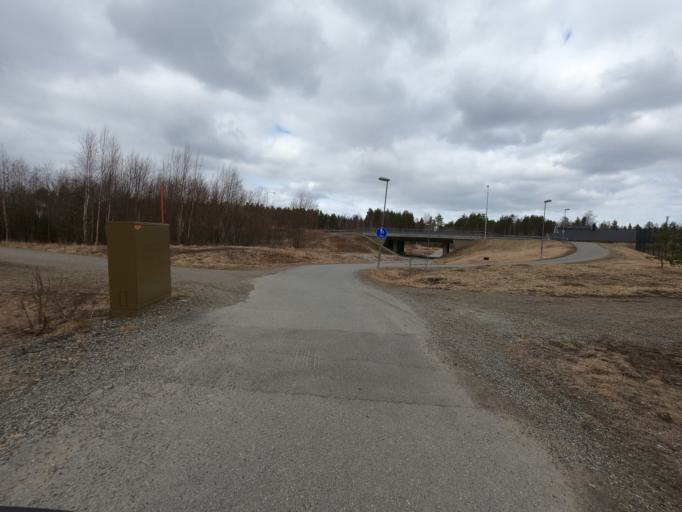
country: FI
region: North Karelia
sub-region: Joensuu
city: Joensuu
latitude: 62.5705
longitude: 29.8131
